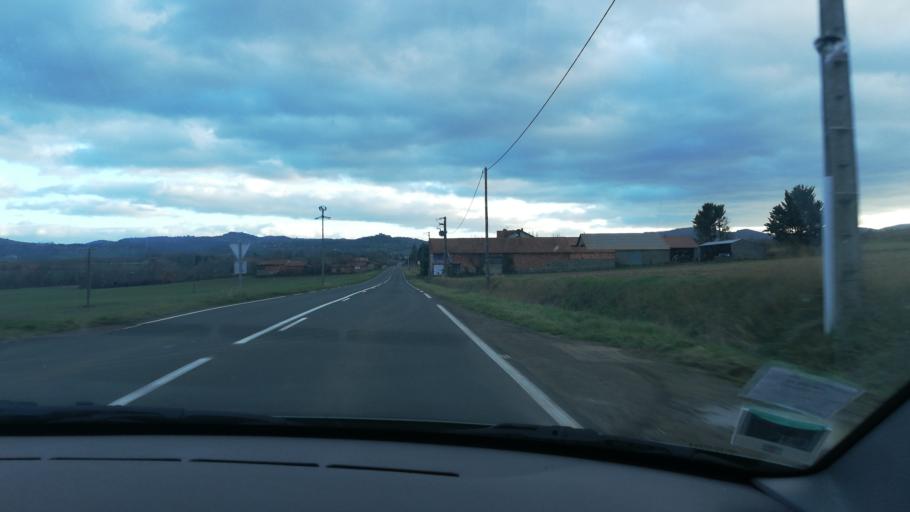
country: FR
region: Auvergne
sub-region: Departement du Puy-de-Dome
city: Billom
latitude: 45.7394
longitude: 3.3335
